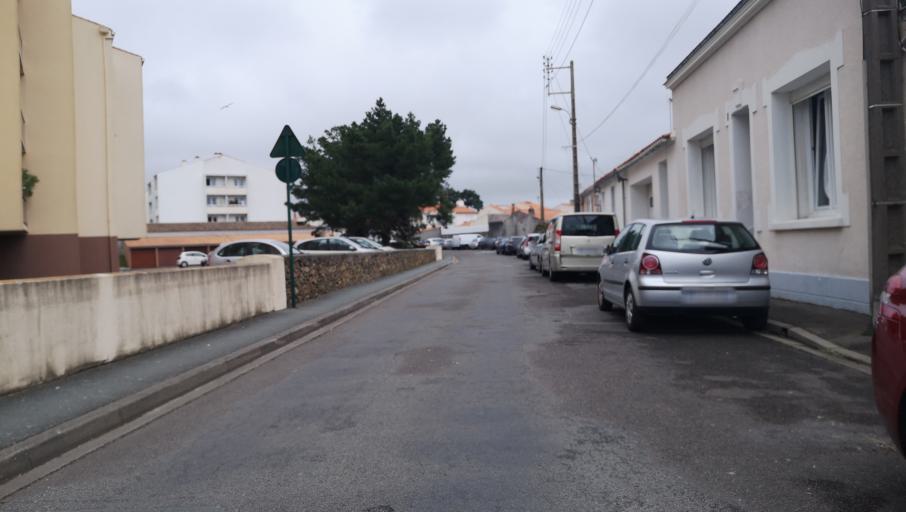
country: FR
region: Pays de la Loire
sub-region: Departement de la Vendee
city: Les Sables-d'Olonne
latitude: 46.5023
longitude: -1.7832
